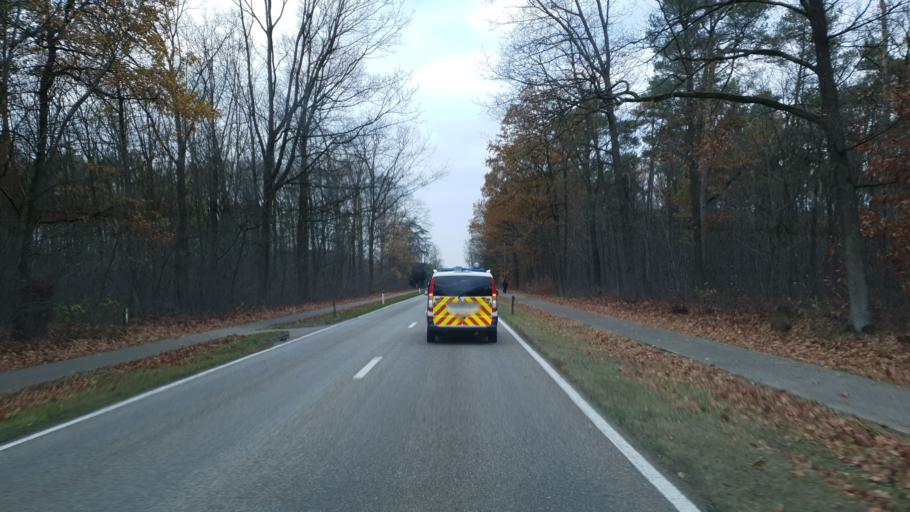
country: BE
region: Flanders
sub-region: Provincie Limburg
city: Lanaken
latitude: 50.9158
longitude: 5.6129
